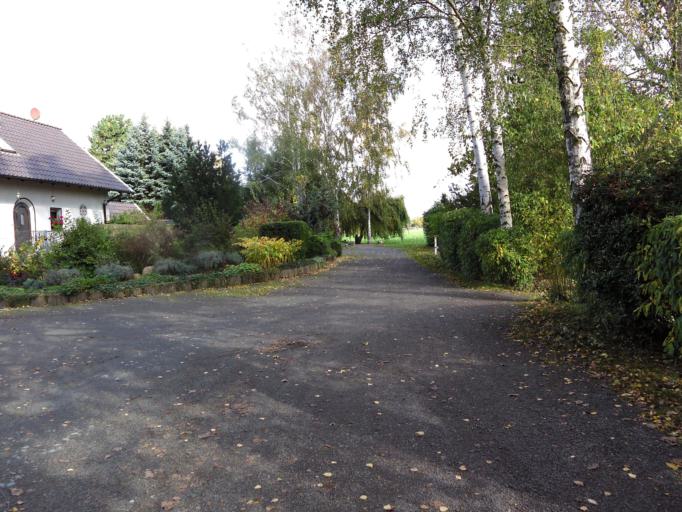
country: DE
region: Saxony
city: Grossposna
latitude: 51.3026
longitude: 12.4552
